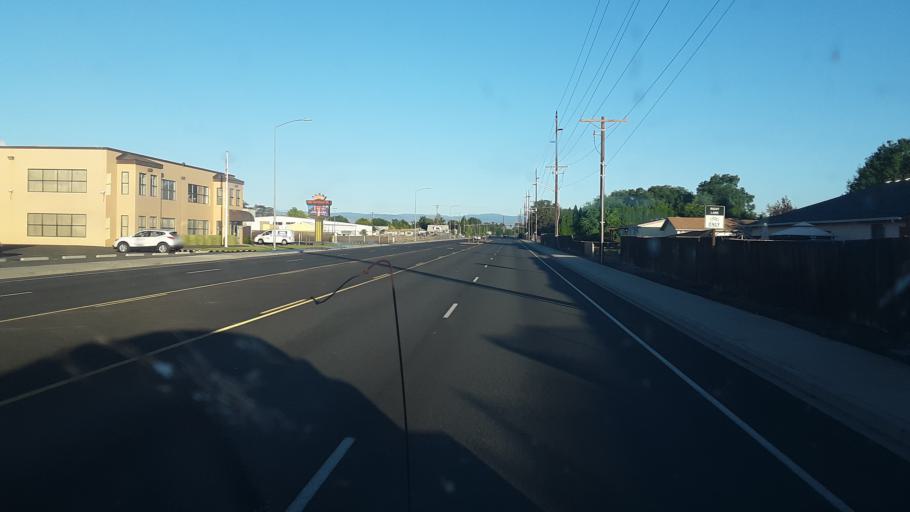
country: US
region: Washington
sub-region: Yakima County
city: Union Gap
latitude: 46.5634
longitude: -120.5046
